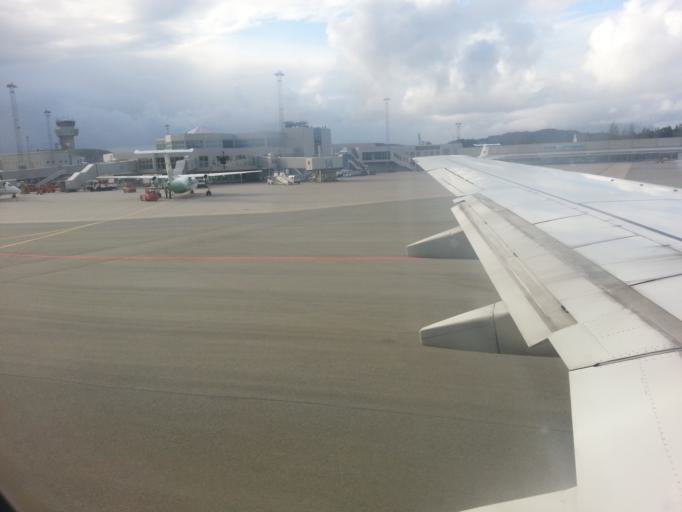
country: NO
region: Nordland
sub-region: Bodo
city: Bodo
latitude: 67.2708
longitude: 14.3685
